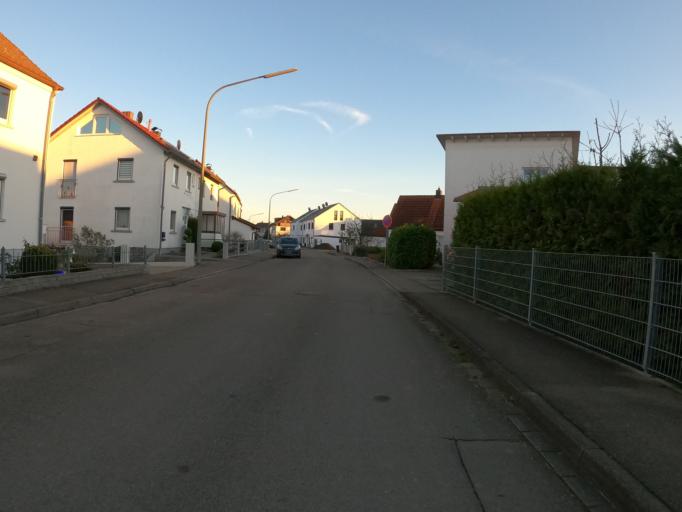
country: DE
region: Bavaria
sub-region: Swabia
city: Holzheim
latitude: 48.4191
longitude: 10.0626
